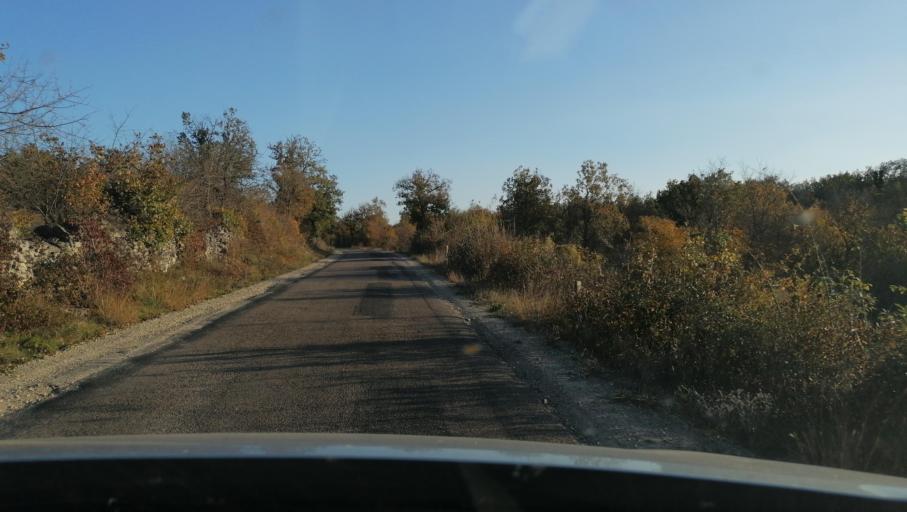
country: FR
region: Midi-Pyrenees
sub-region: Departement du Lot
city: Vayrac
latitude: 44.8724
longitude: 1.6633
